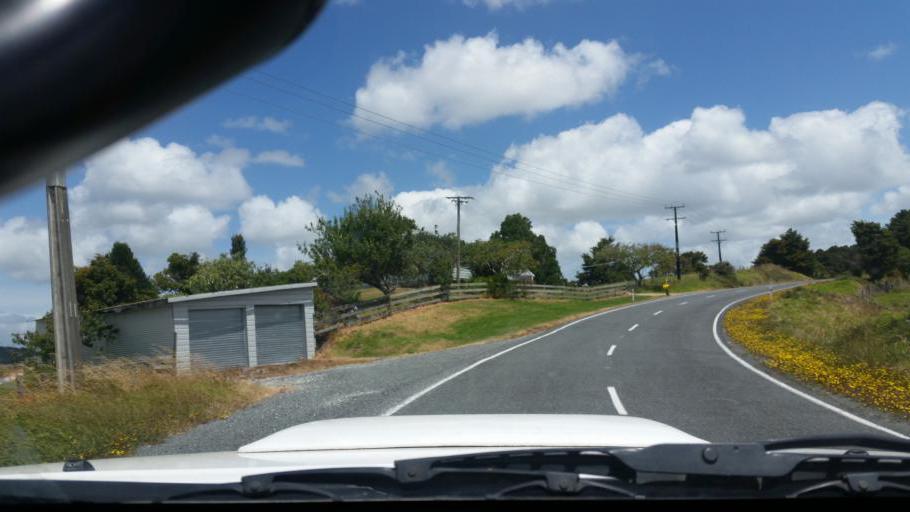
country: NZ
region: Northland
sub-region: Whangarei
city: Ruakaka
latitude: -36.0596
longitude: 174.2728
